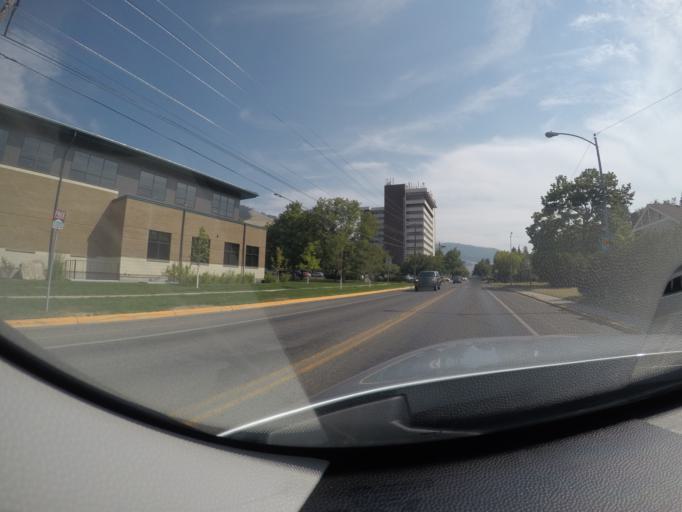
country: US
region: Montana
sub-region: Missoula County
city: Missoula
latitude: 46.8625
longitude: -113.9893
